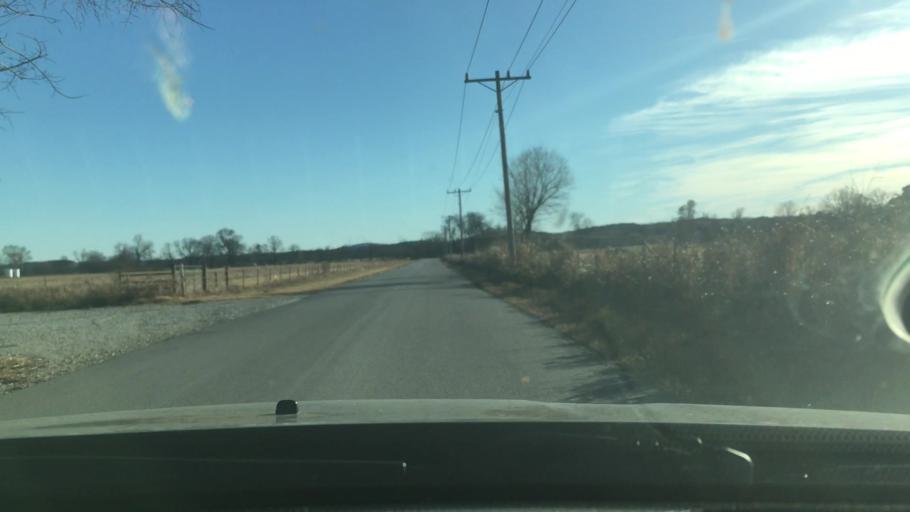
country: US
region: Oklahoma
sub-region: Murray County
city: Davis
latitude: 34.5032
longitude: -97.1559
